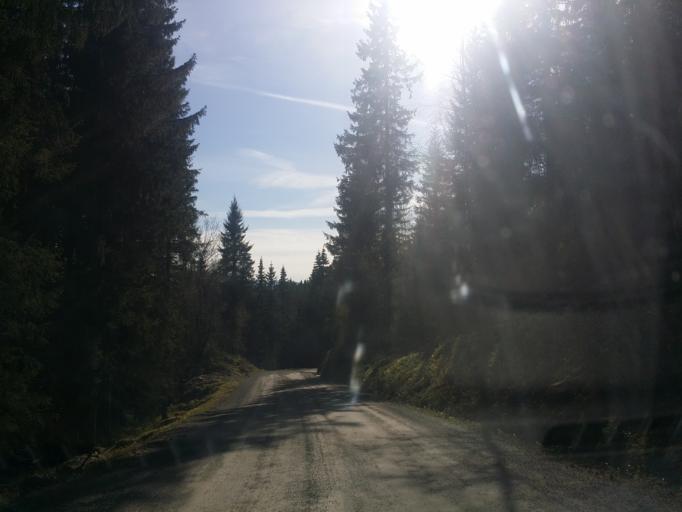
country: NO
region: Telemark
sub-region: Seljord
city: Seljord
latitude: 59.6192
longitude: 8.6875
